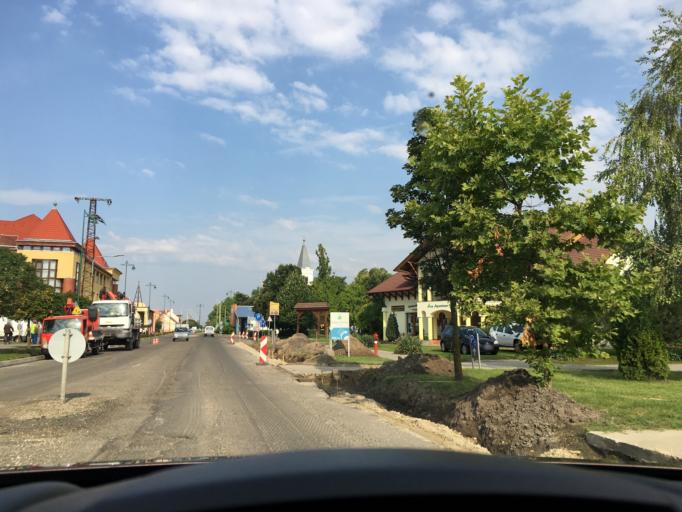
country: HU
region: Csongrad
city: Morahalom
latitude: 46.2162
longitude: 19.8926
